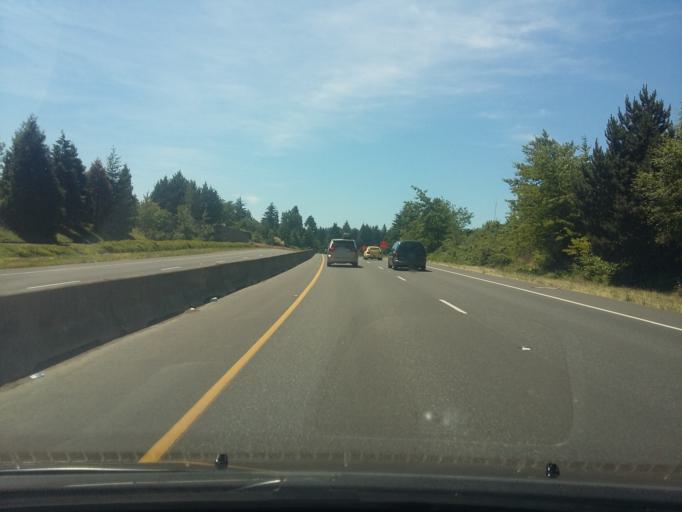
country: US
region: Washington
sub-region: Clark County
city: Five Corners
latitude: 45.6823
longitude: -122.5643
